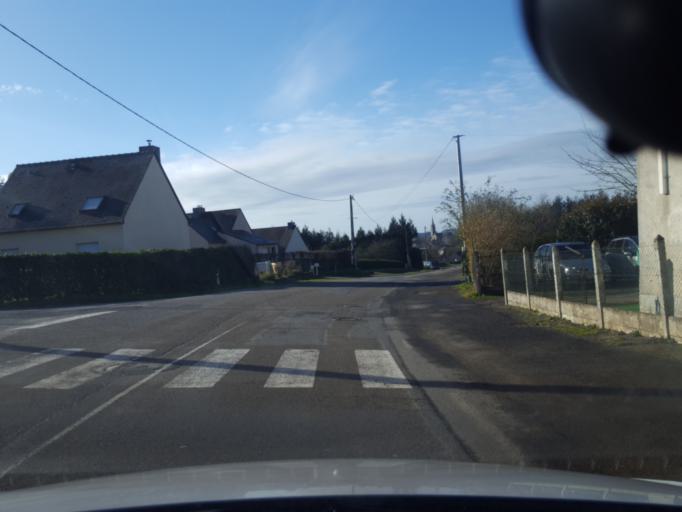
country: FR
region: Brittany
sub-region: Departement d'Ille-et-Vilaine
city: Guignen
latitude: 47.9272
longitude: -1.8534
